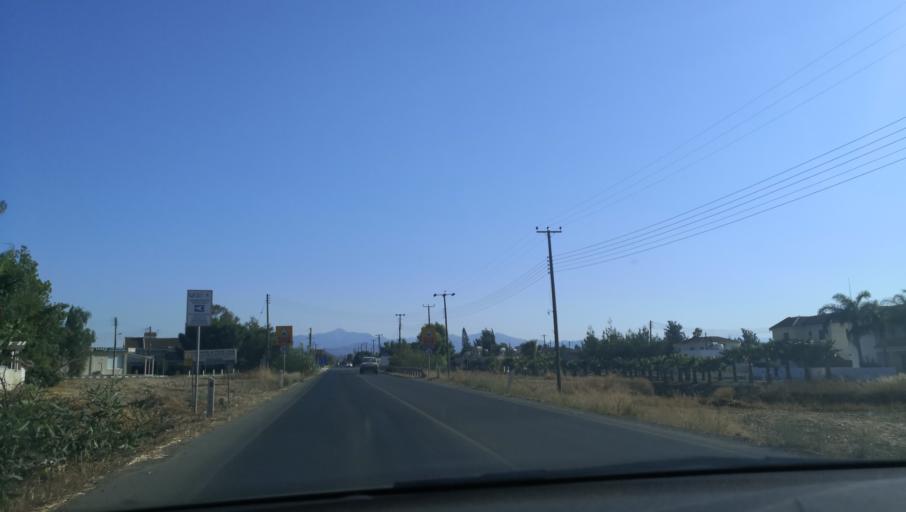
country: CY
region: Lefkosia
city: Psimolofou
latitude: 35.0627
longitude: 33.2654
